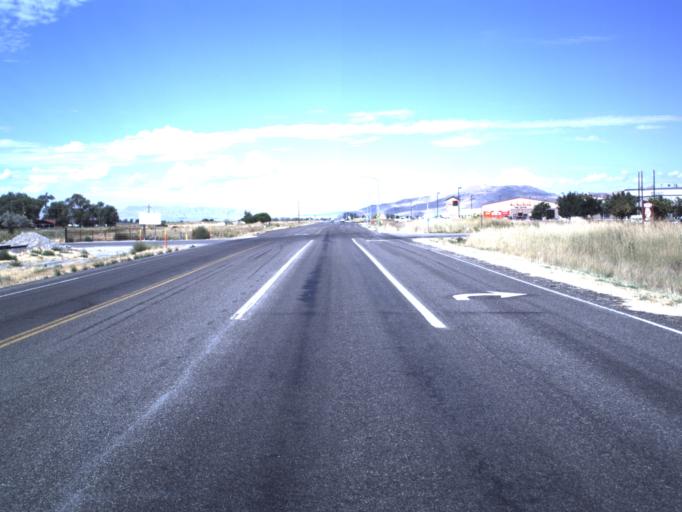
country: US
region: Utah
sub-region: Box Elder County
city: Honeyville
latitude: 41.5540
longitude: -112.1241
